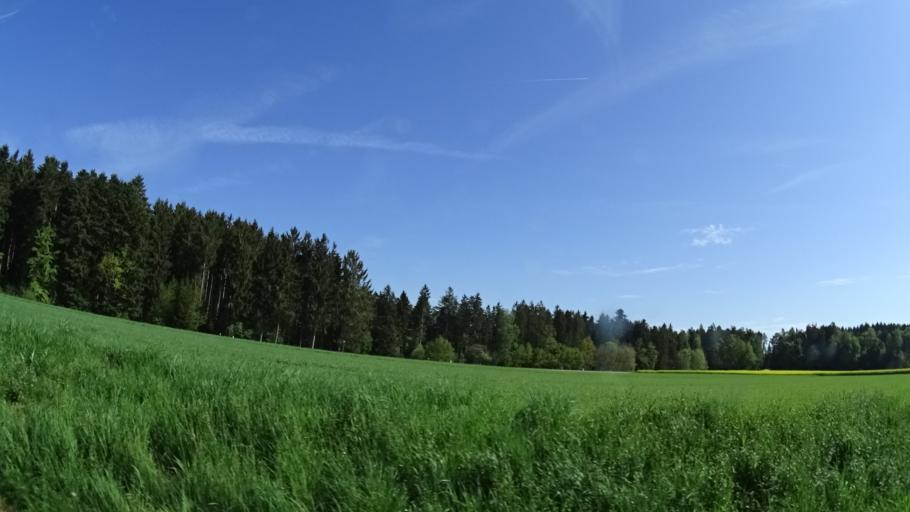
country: DE
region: Baden-Wuerttemberg
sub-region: Karlsruhe Region
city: Neuweiler
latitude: 48.6366
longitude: 8.6078
